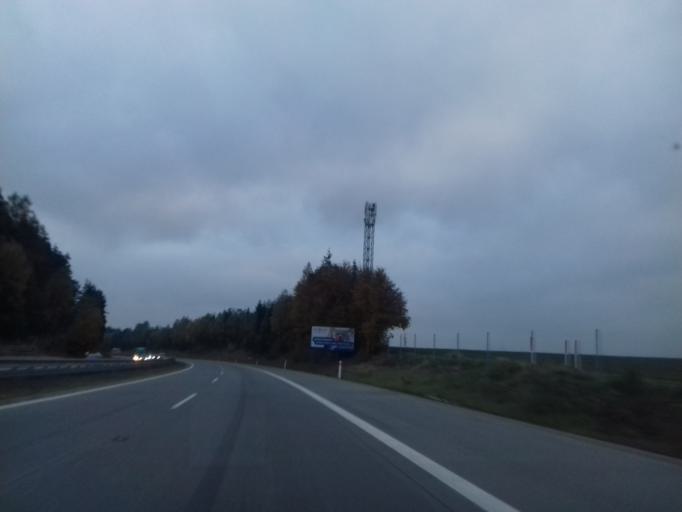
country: CZ
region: Central Bohemia
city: Cechtice
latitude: 49.6156
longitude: 15.1366
